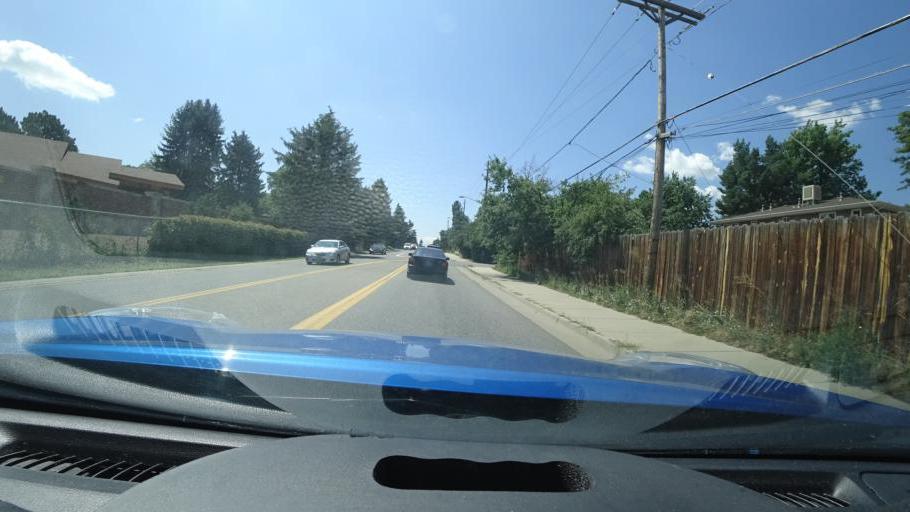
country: US
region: Colorado
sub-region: Arapahoe County
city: Glendale
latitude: 39.7079
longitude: -104.9035
